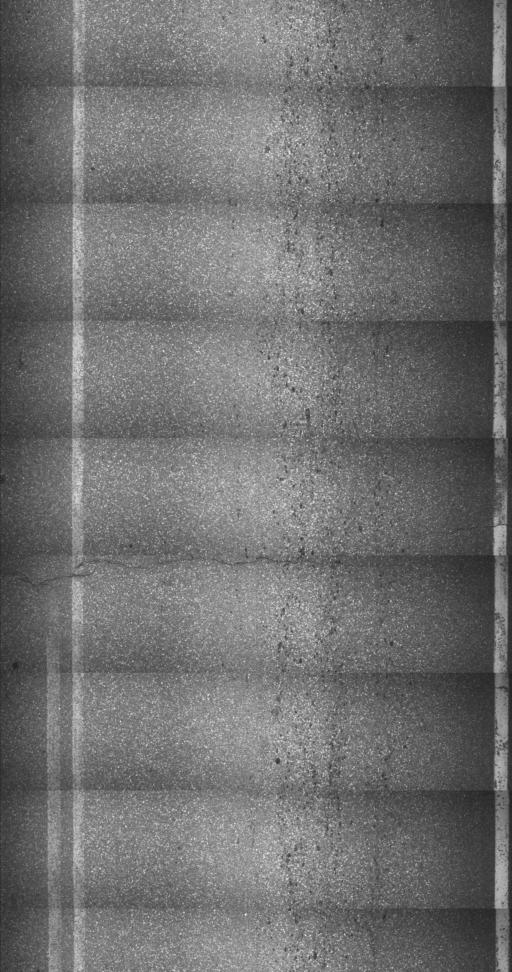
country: US
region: Vermont
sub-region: Orleans County
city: Newport
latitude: 44.8920
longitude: -72.0563
